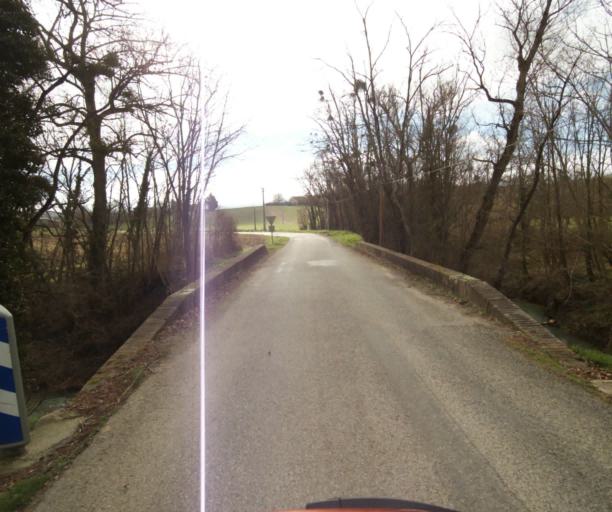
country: FR
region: Midi-Pyrenees
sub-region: Departement de l'Ariege
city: Pamiers
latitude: 43.1070
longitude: 1.5478
